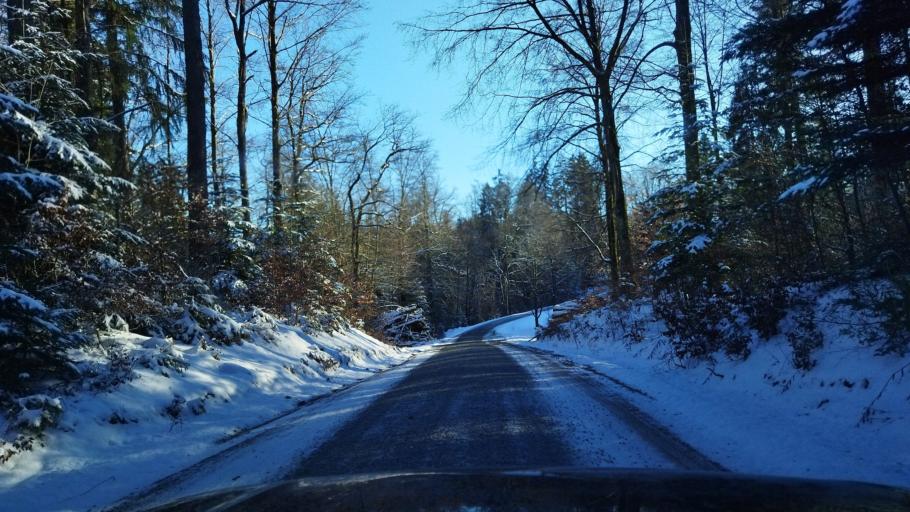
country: DE
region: Baden-Wuerttemberg
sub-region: Regierungsbezirk Stuttgart
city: Gerabronn
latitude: 48.9625
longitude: 9.9171
